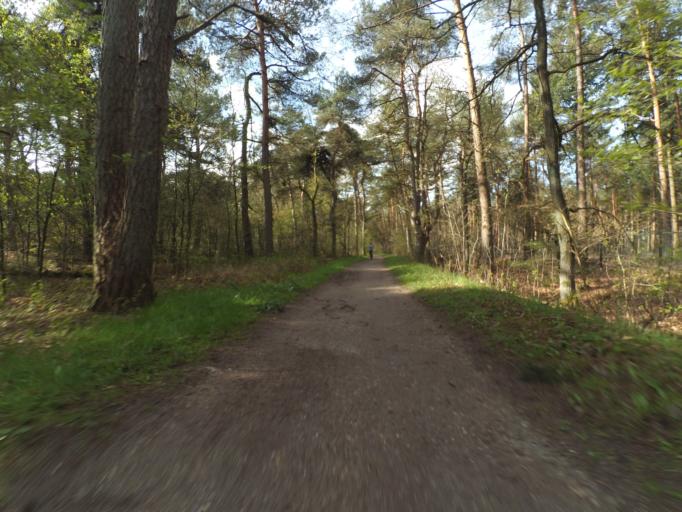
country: NL
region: Utrecht
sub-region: Gemeente Utrechtse Heuvelrug
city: Driebergen-Rijsenburg
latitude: 52.0596
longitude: 5.3073
